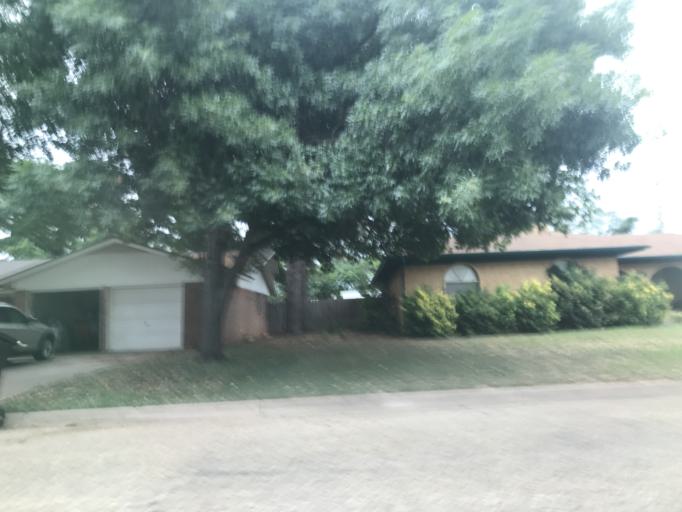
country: US
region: Texas
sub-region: Taylor County
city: Abilene
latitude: 32.4126
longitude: -99.7859
